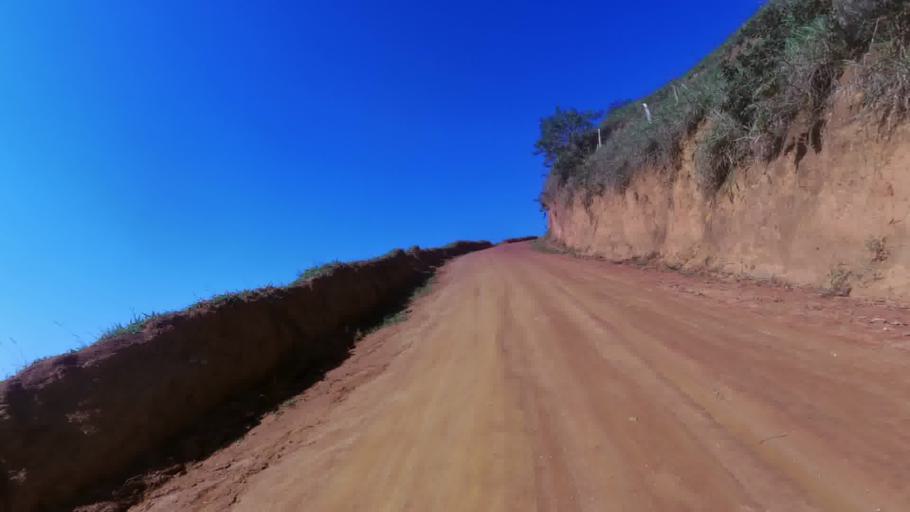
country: BR
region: Espirito Santo
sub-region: Alfredo Chaves
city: Alfredo Chaves
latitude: -20.6809
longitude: -40.7786
